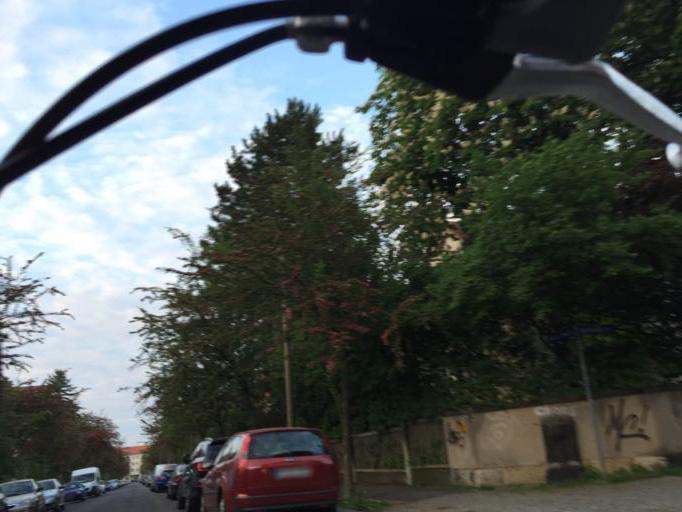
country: DE
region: Saxony
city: Dresden
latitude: 51.0322
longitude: 13.7161
